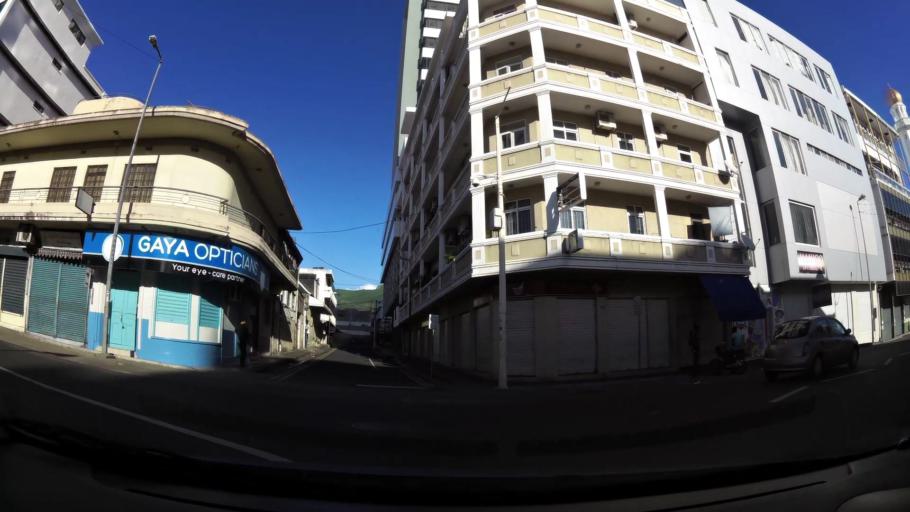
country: MU
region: Port Louis
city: Port Louis
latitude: -20.1623
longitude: 57.5065
